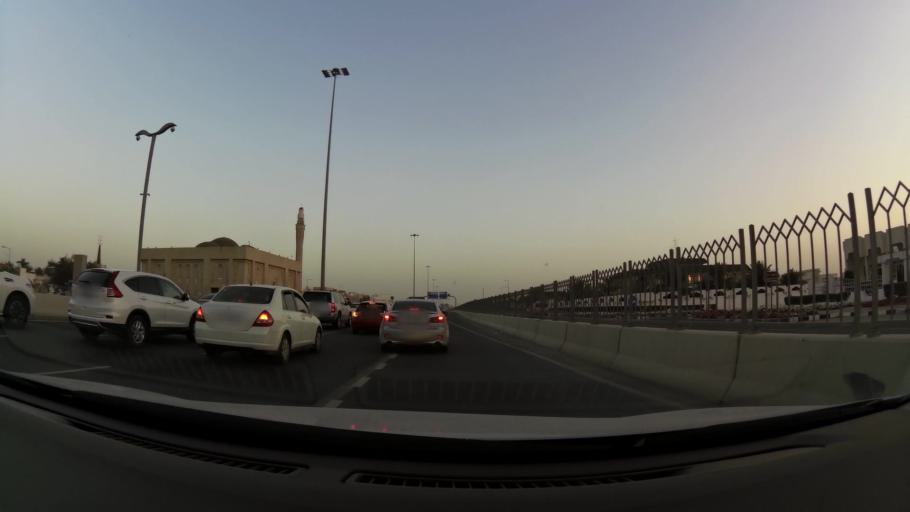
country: QA
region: Baladiyat ar Rayyan
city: Ar Rayyan
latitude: 25.3151
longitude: 51.4709
